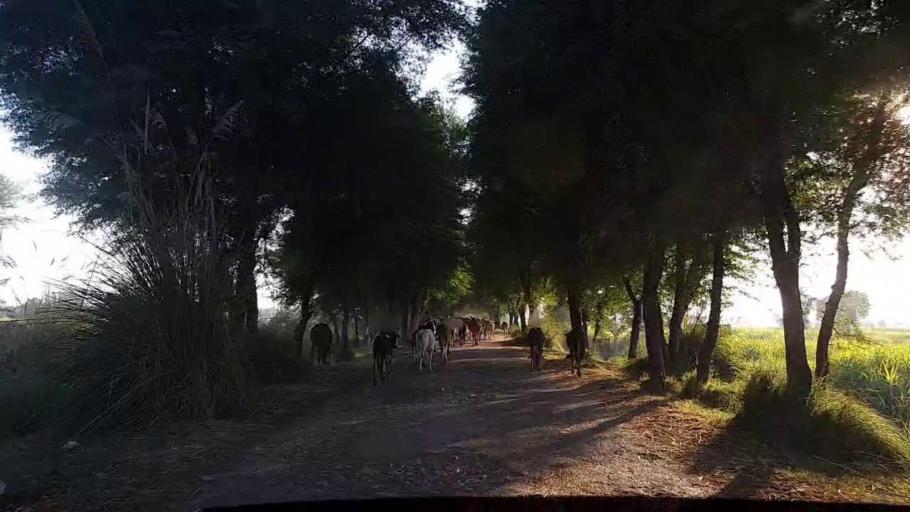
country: PK
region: Sindh
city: Sobhadero
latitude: 27.4085
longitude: 68.3933
